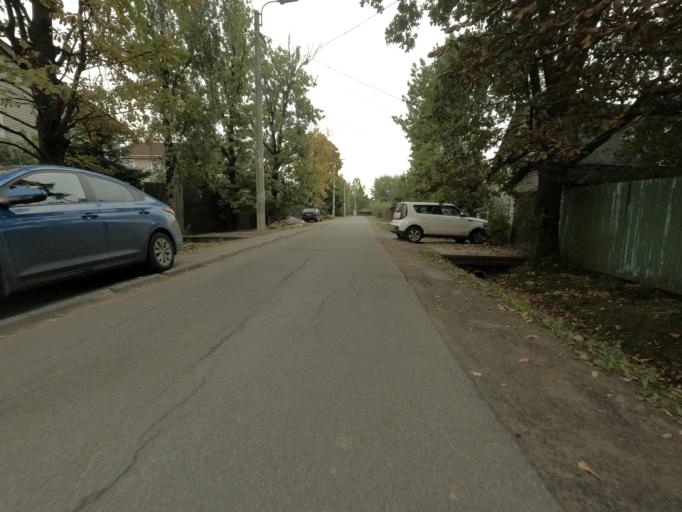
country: RU
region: St.-Petersburg
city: Ust'-Izhora
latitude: 59.8125
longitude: 30.5868
